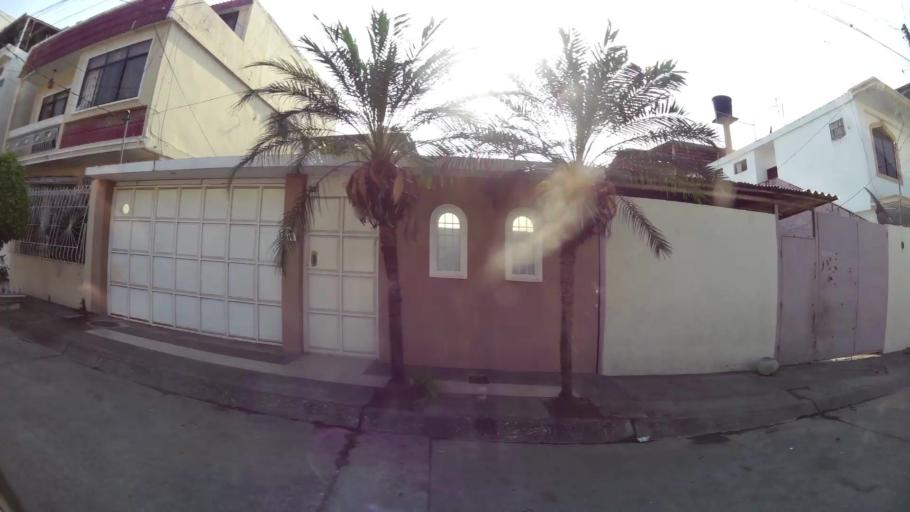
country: EC
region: Guayas
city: Guayaquil
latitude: -2.1499
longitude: -79.9099
